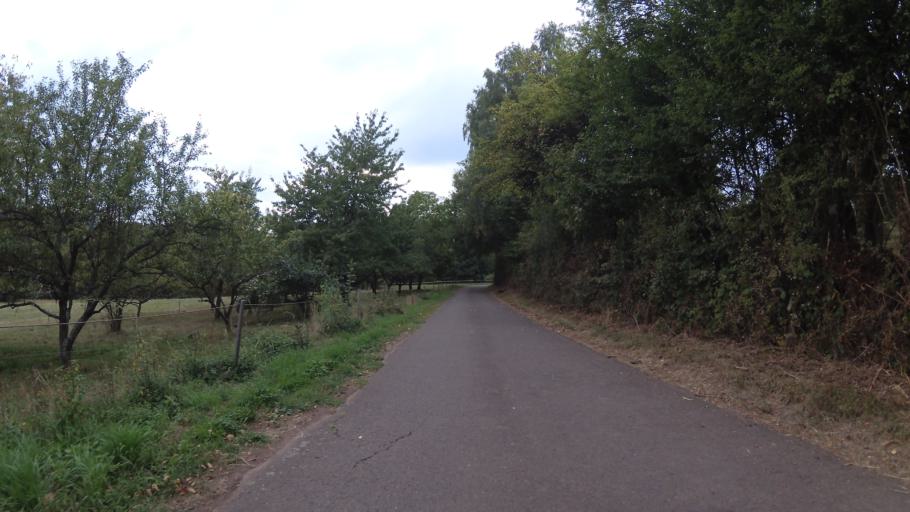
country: DE
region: Saarland
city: Ottweiler
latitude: 49.4136
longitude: 7.1432
